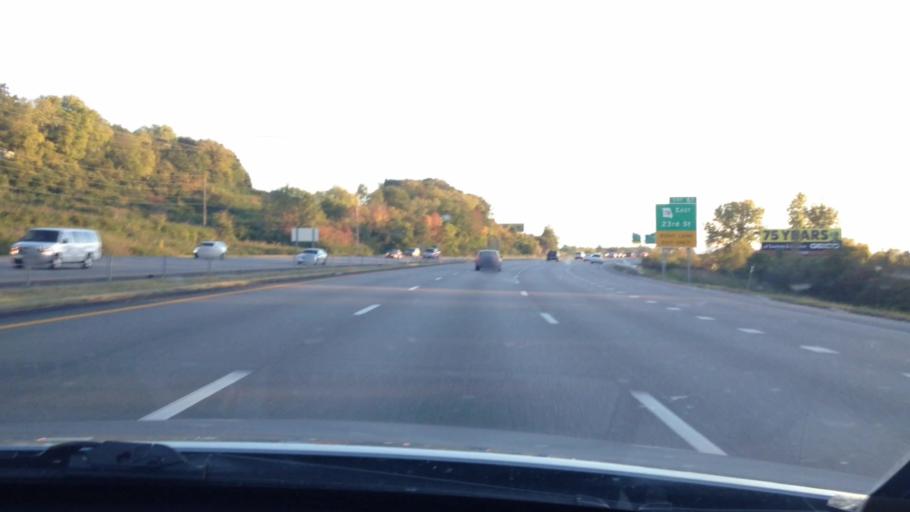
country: US
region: Missouri
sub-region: Jackson County
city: Sugar Creek
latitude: 39.0875
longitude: -94.4877
